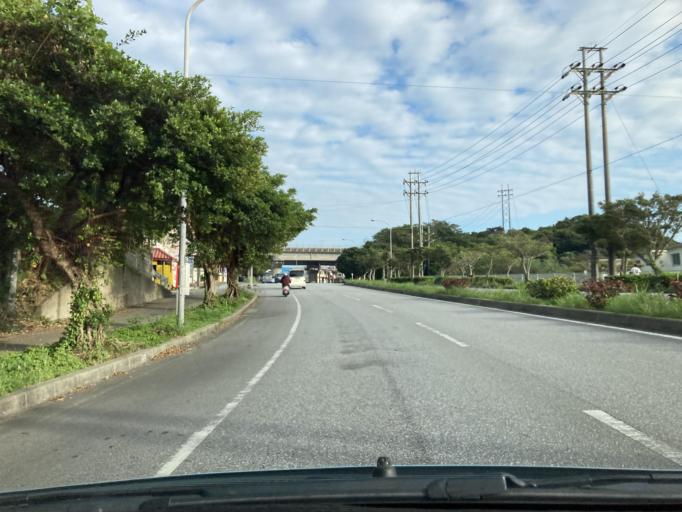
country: JP
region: Okinawa
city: Okinawa
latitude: 26.3570
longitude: 127.8026
